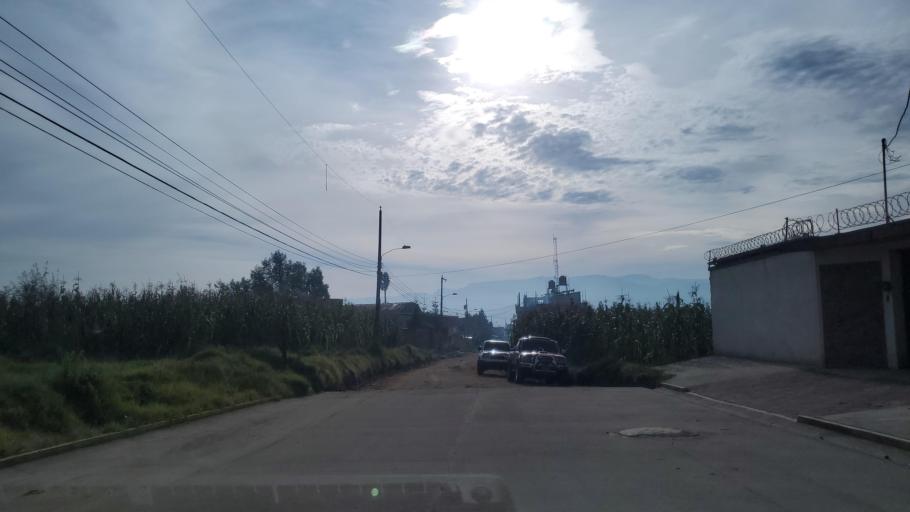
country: GT
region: Quetzaltenango
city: Quetzaltenango
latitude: 14.8416
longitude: -91.5462
